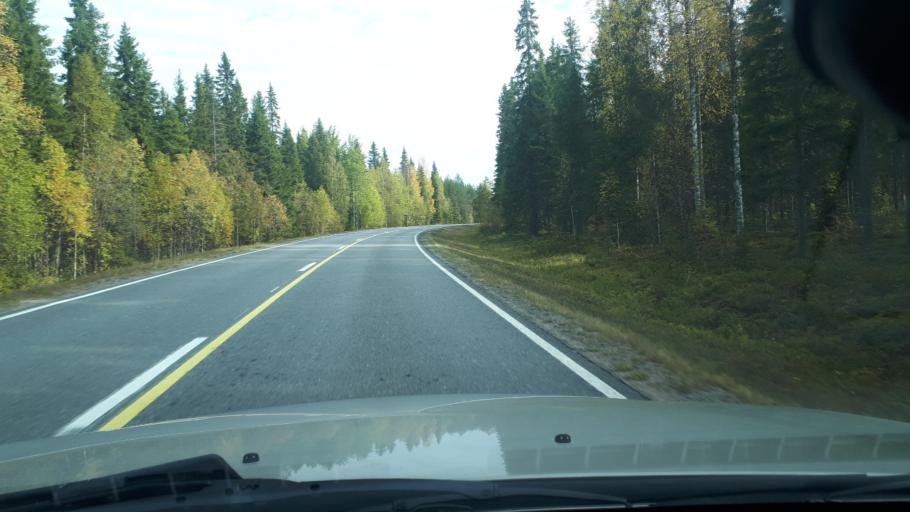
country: FI
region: Northern Ostrobothnia
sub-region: Oulu
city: Yli-Ii
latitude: 65.9506
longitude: 25.9104
